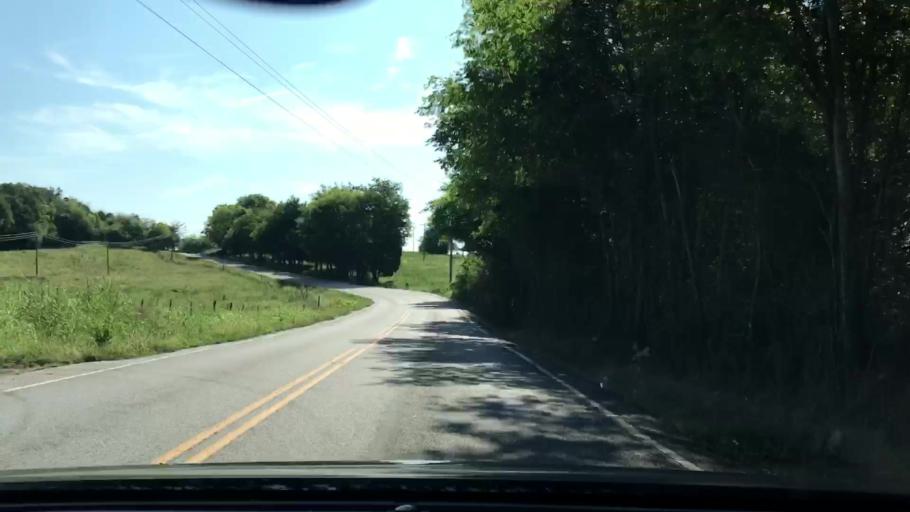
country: US
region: Tennessee
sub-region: Jackson County
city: Gainesboro
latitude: 36.3546
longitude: -85.7179
